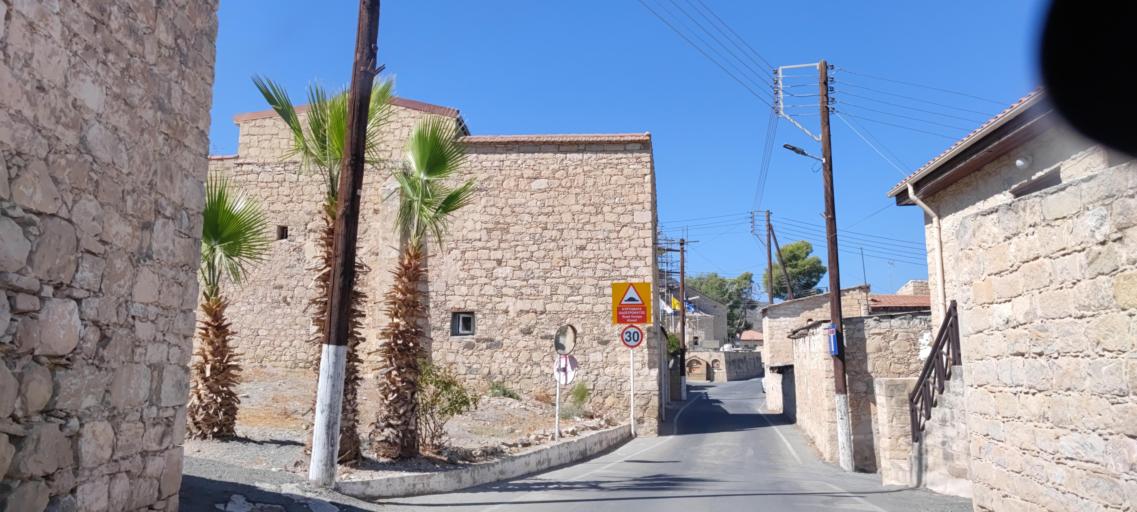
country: CY
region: Limassol
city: Mouttagiaka
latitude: 34.7531
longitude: 33.0981
